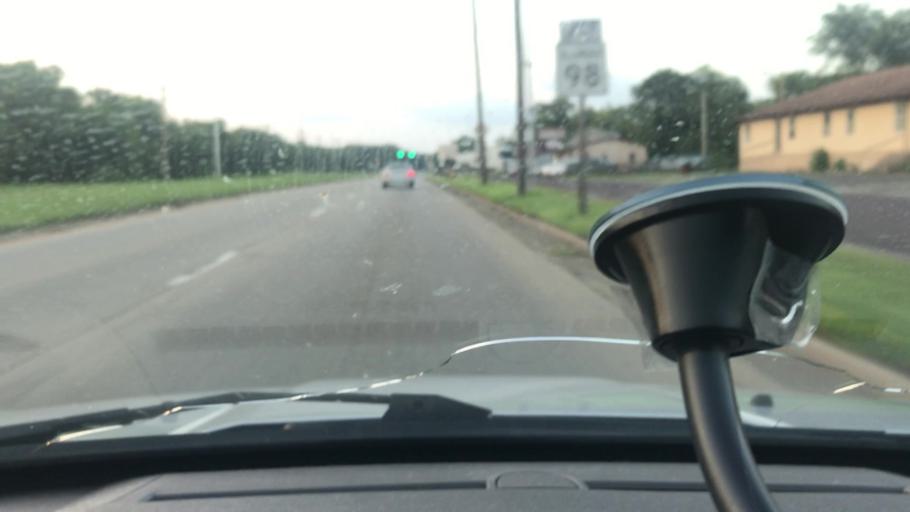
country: US
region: Illinois
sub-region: Tazewell County
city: North Pekin
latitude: 40.6020
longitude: -89.6375
